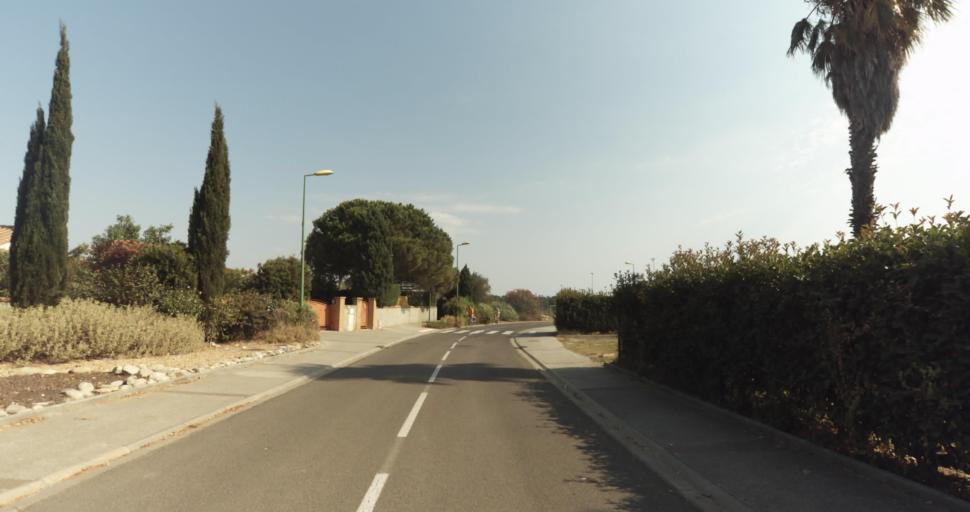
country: FR
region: Languedoc-Roussillon
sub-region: Departement des Pyrenees-Orientales
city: Latour-Bas-Elne
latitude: 42.6081
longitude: 3.0061
